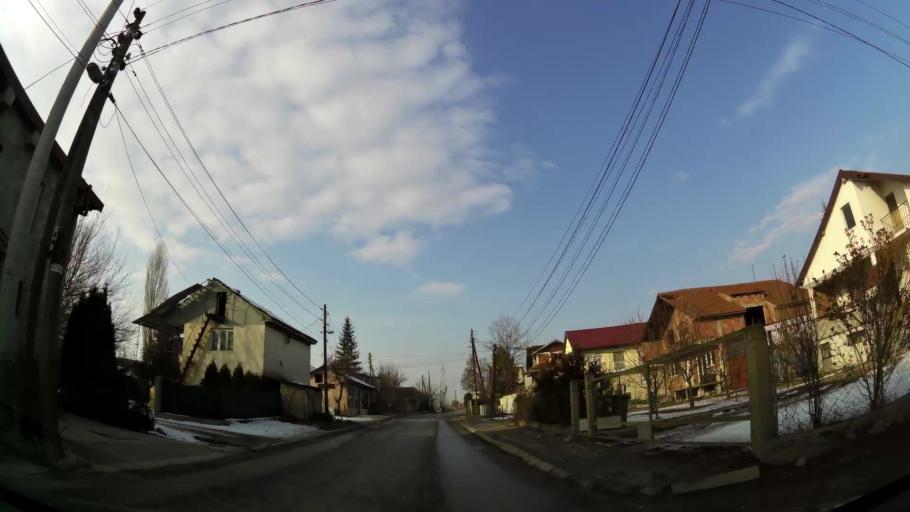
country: MK
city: Creshevo
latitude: 42.0287
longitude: 21.5127
